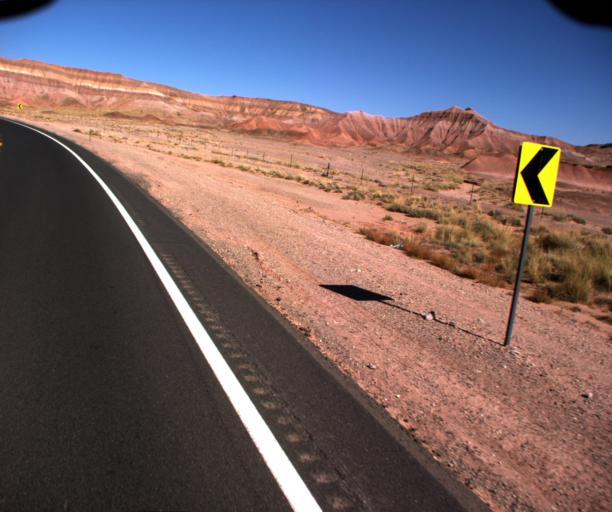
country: US
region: Arizona
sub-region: Coconino County
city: Tuba City
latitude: 36.0823
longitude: -111.3691
